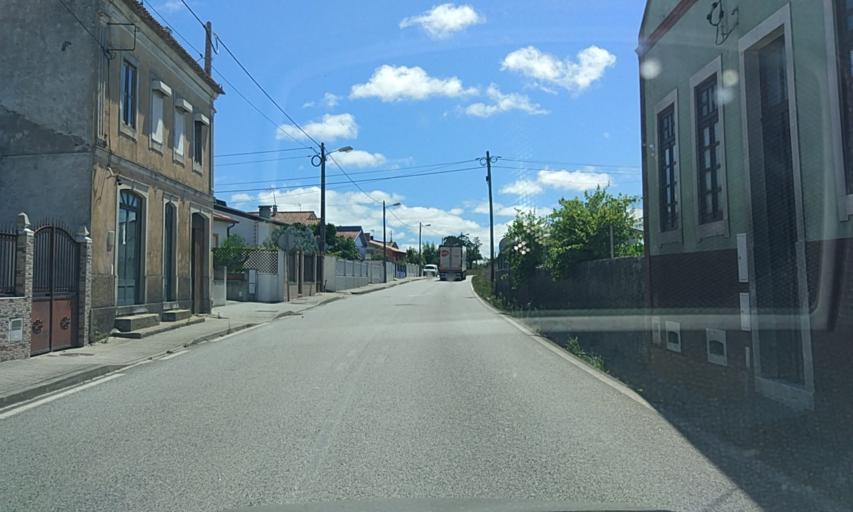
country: PT
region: Coimbra
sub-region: Mira
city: Mira
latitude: 40.4218
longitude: -8.7376
